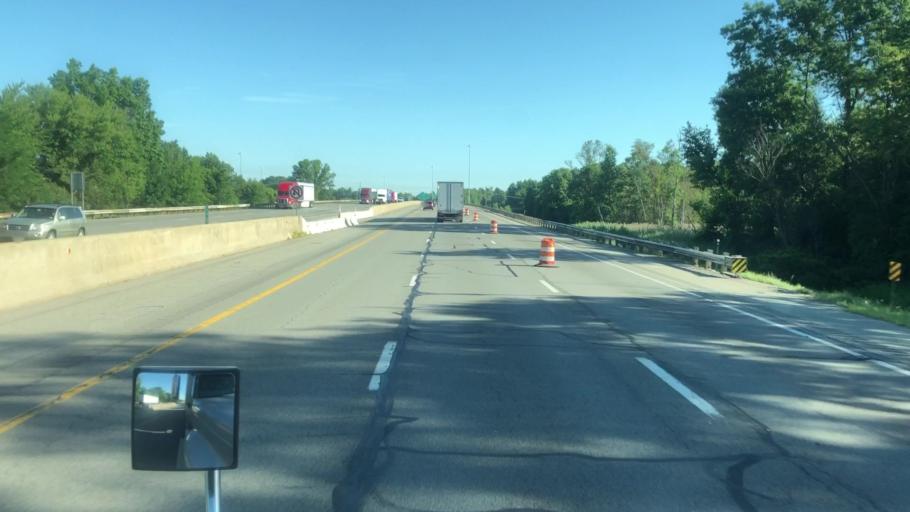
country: US
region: Ohio
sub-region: Trumbull County
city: Newton Falls
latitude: 41.2102
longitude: -80.9493
